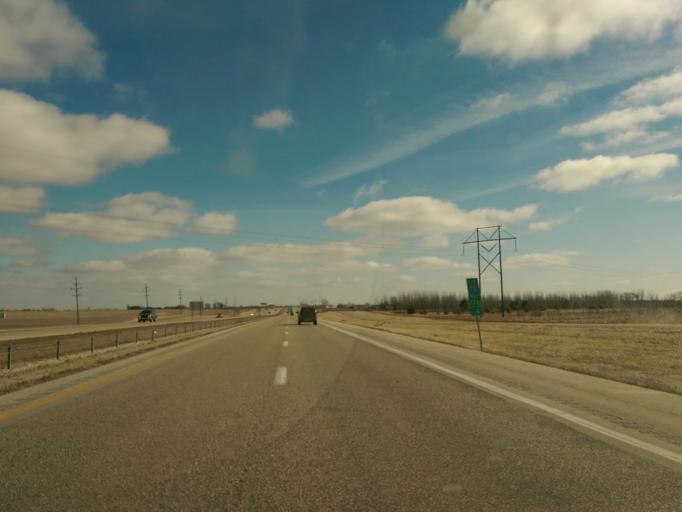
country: US
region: Missouri
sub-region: Montgomery County
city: Montgomery City
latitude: 38.8933
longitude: -91.4344
